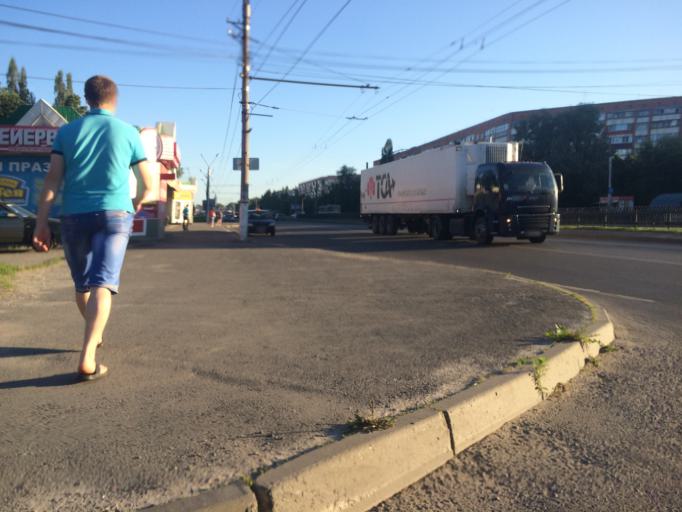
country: RU
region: Kursk
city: Kursk
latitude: 51.6719
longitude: 36.1435
